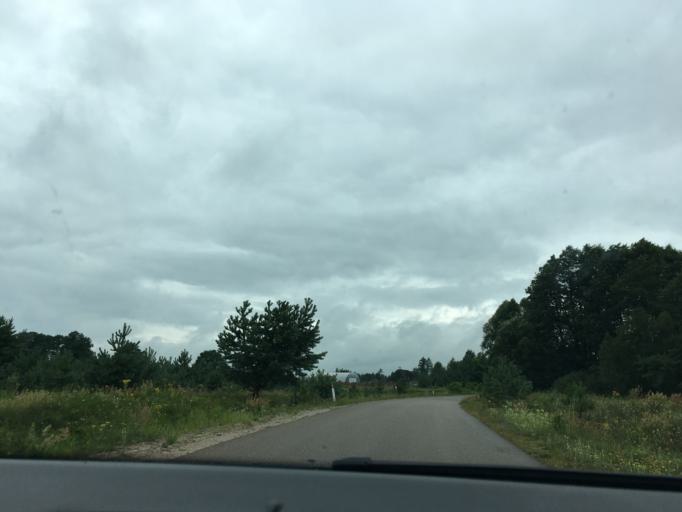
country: PL
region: Podlasie
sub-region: Powiat sejnenski
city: Krasnopol
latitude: 54.0910
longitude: 23.2402
